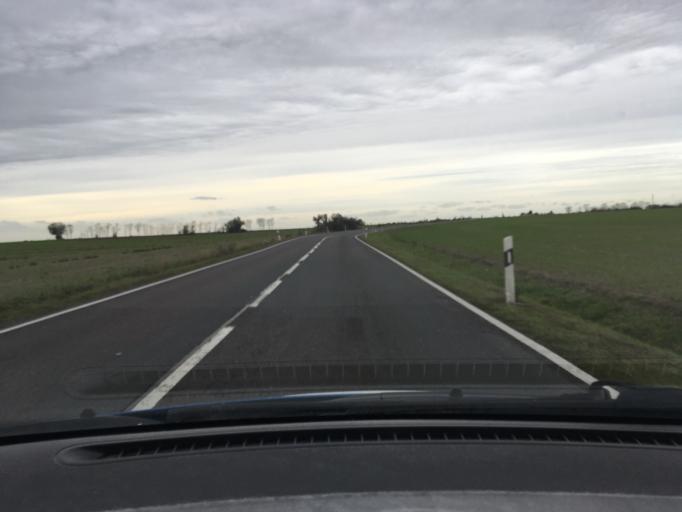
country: DE
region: Saxony-Anhalt
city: Leitzkau
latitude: 52.0391
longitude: 11.9792
